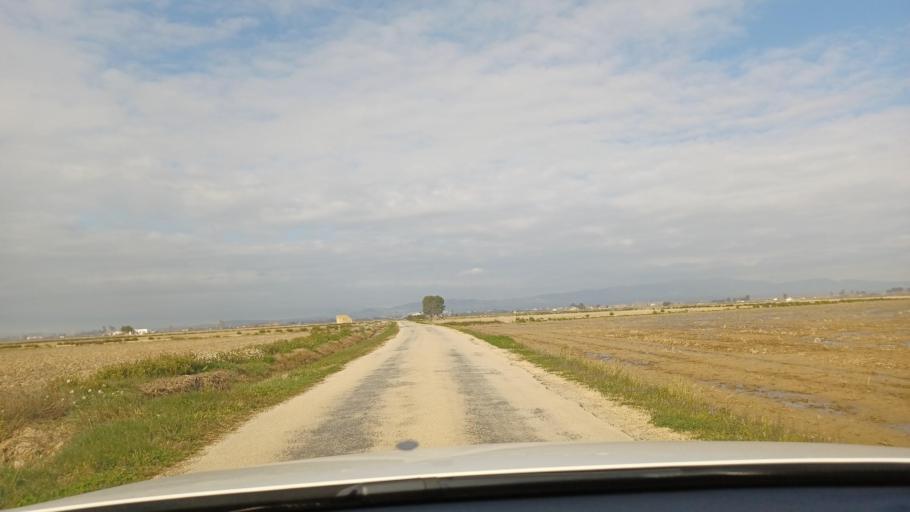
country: ES
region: Catalonia
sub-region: Provincia de Tarragona
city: Deltebre
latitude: 40.6932
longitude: 0.6516
